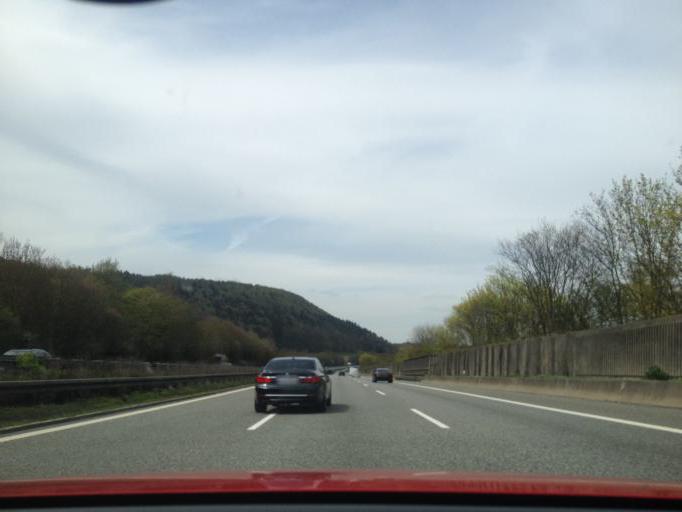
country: DE
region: Bavaria
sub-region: Regierungsbezirk Mittelfranken
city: Greding
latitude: 49.0275
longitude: 11.3661
